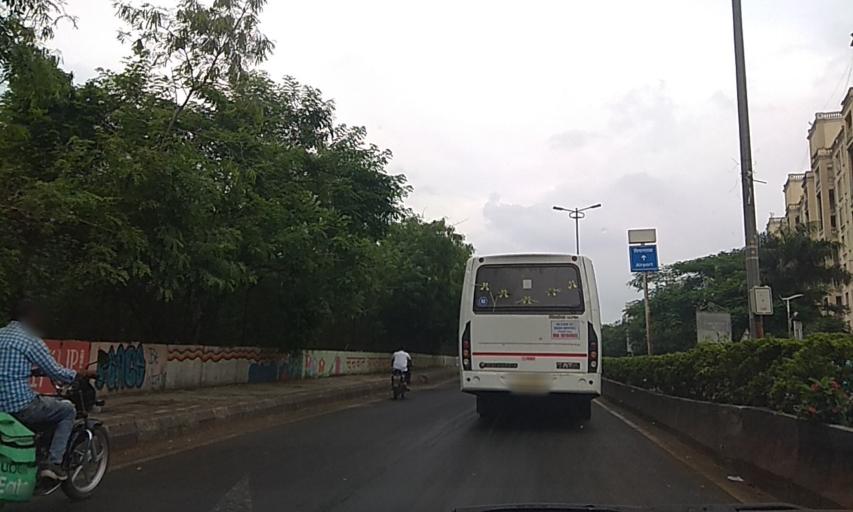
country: IN
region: Maharashtra
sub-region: Pune Division
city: Lohogaon
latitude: 18.5652
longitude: 73.9070
